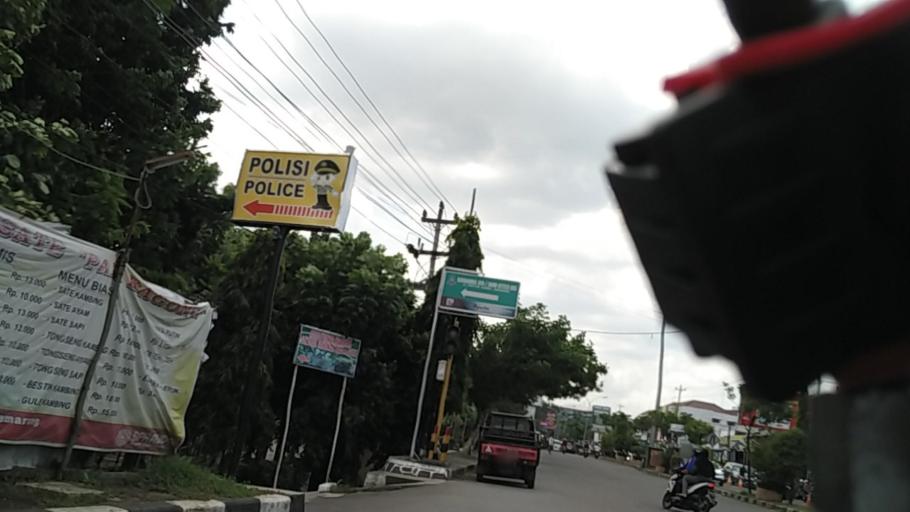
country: ID
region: Central Java
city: Semarang
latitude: -6.9963
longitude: 110.3475
